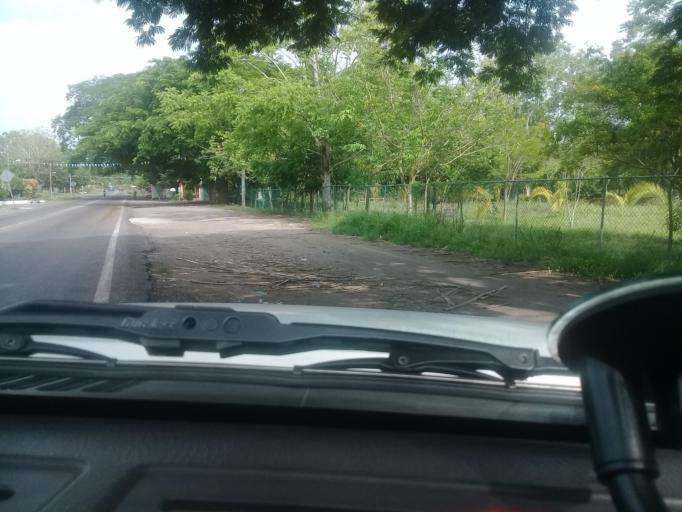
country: MX
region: Veracruz
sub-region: Paso de Ovejas
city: Tolome
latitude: 19.2656
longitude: -96.3765
